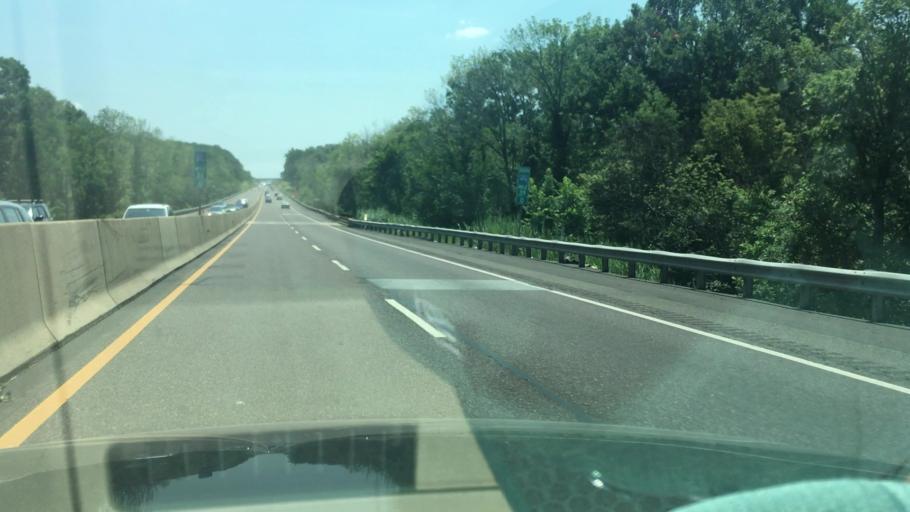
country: US
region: Pennsylvania
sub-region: Montgomery County
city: Woxall
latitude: 40.3705
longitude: -75.4017
